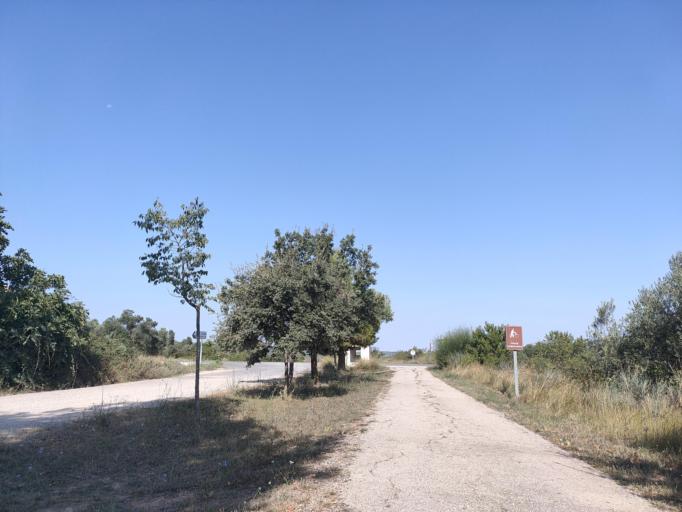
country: ES
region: Catalonia
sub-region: Provincia de Tarragona
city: Horta de Sant Joan
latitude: 40.9654
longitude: 0.3186
